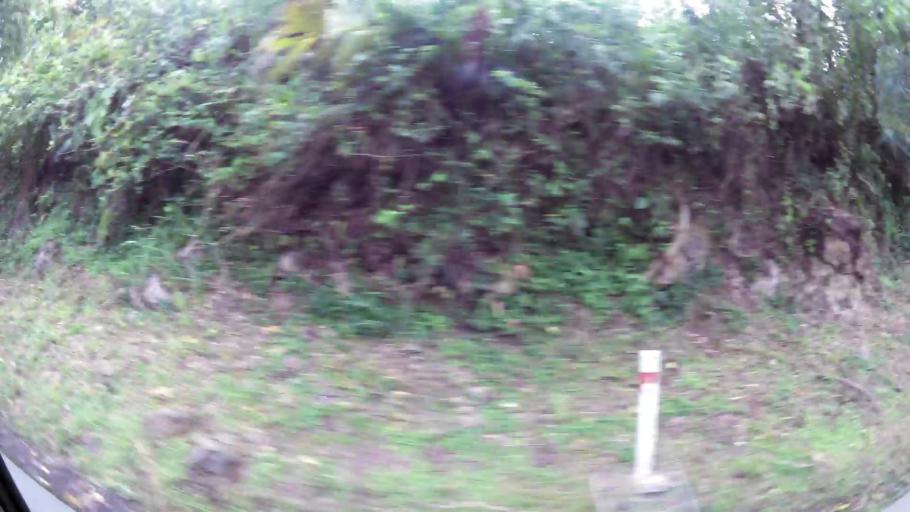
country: EC
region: Santo Domingo de los Tsachilas
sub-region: Canton Santo Domingo de los Colorados
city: Santo Domingo de los Colorados
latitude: -0.2829
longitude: -79.0698
